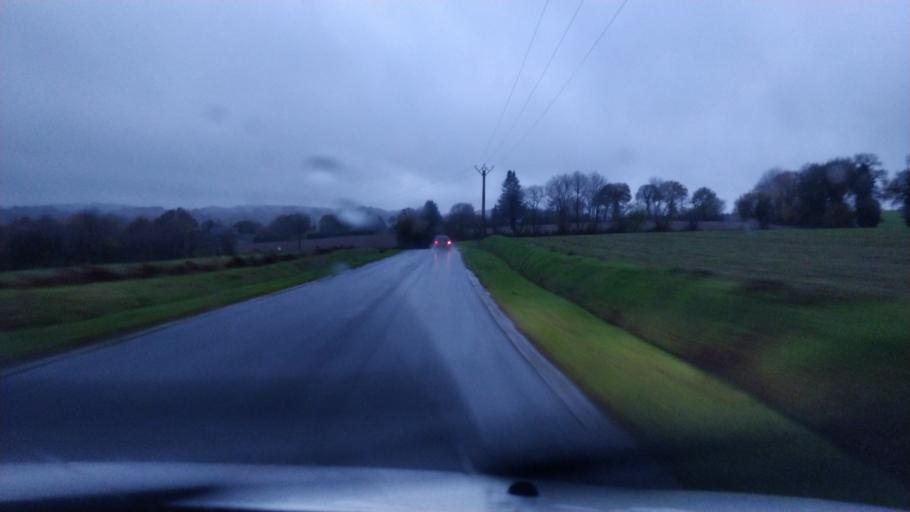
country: FR
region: Brittany
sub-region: Departement des Cotes-d'Armor
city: Plemet
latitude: 48.1971
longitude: -2.5182
